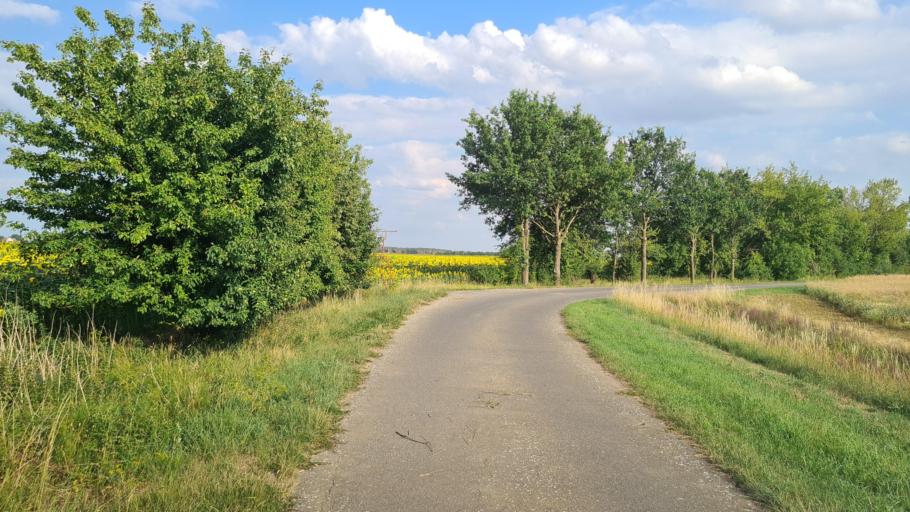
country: DE
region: Saxony-Anhalt
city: Jessen
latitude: 51.7484
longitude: 12.8934
